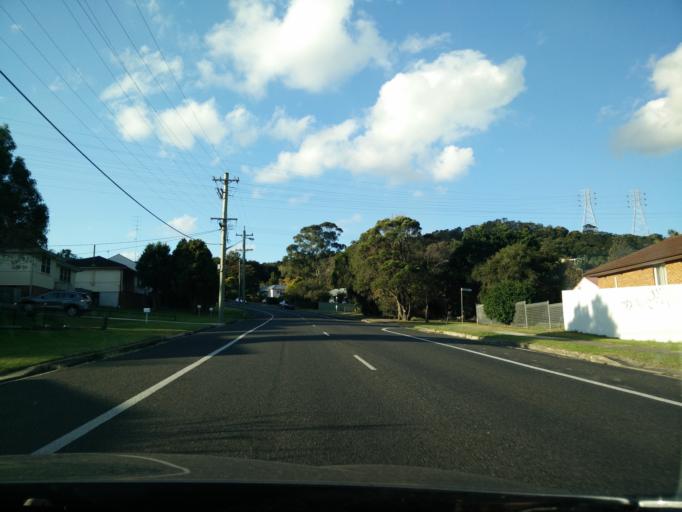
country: AU
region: New South Wales
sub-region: Wollongong
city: Berkeley
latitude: -34.4725
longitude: 150.8433
